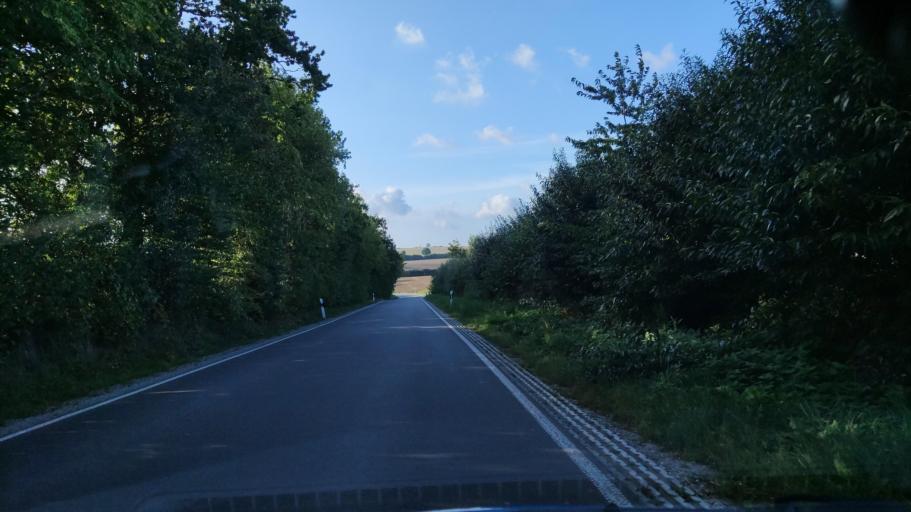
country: DE
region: Schleswig-Holstein
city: Glasau
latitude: 54.0927
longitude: 10.4913
